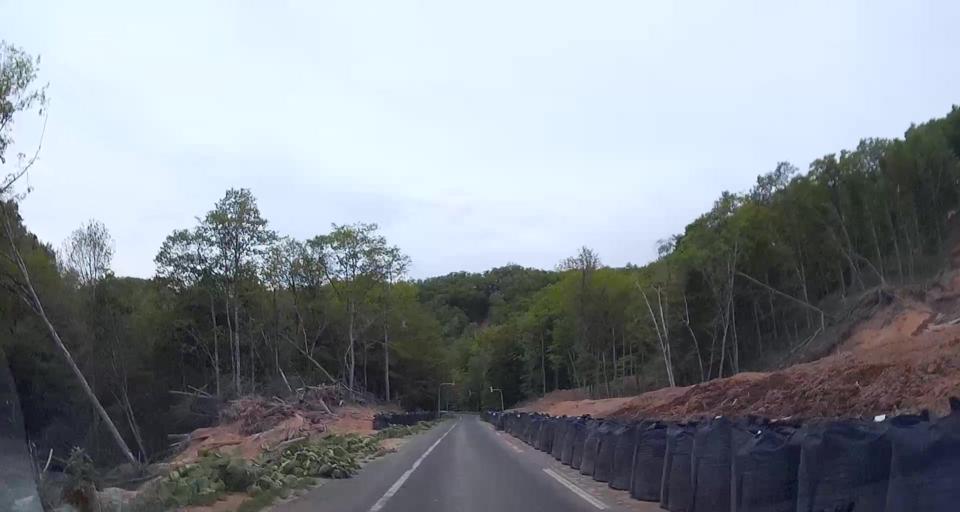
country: JP
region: Hokkaido
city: Chitose
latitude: 42.7915
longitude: 142.0582
